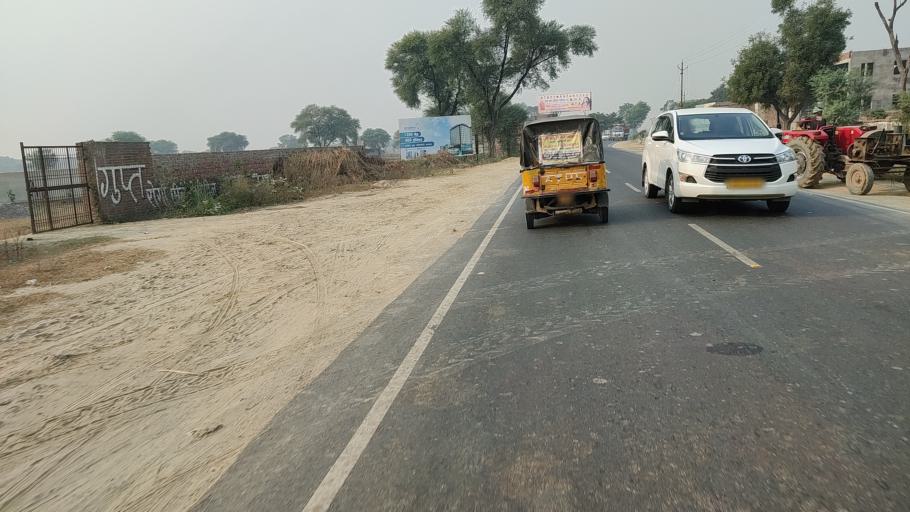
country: IN
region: Uttar Pradesh
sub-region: Mathura
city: Vrindavan
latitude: 27.5589
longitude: 77.7221
